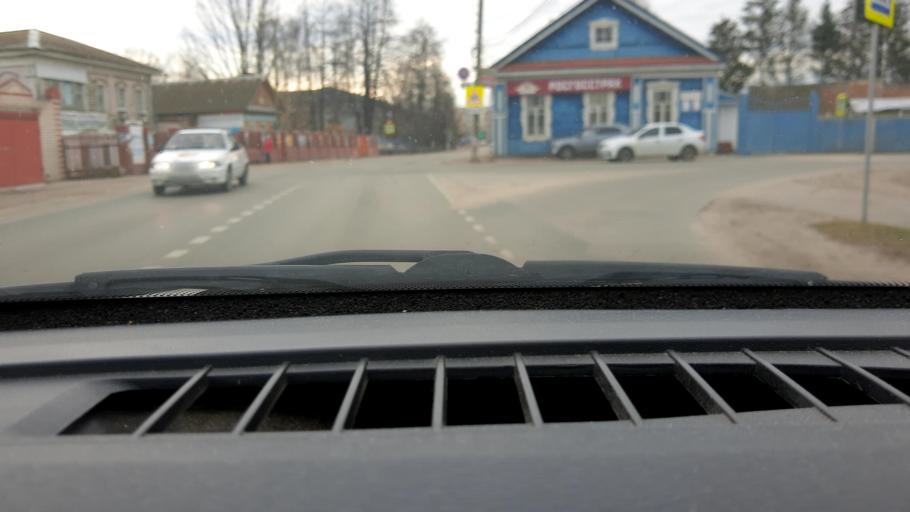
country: RU
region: Nizjnij Novgorod
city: Gorodets
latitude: 56.6431
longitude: 43.4752
